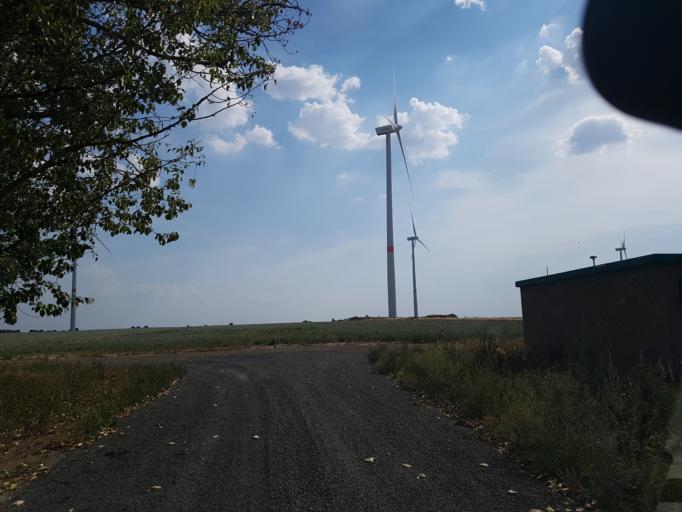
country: DE
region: Brandenburg
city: Treuenbrietzen
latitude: 52.0105
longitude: 12.8618
